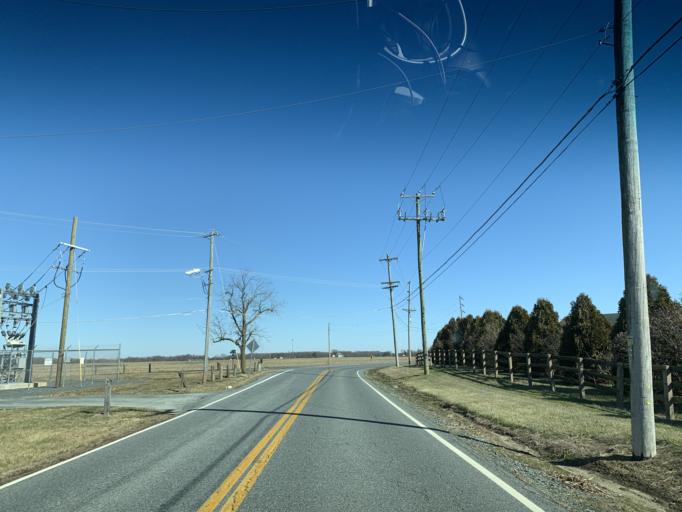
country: US
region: Maryland
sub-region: Cecil County
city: Elkton
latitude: 39.4899
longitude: -75.8559
